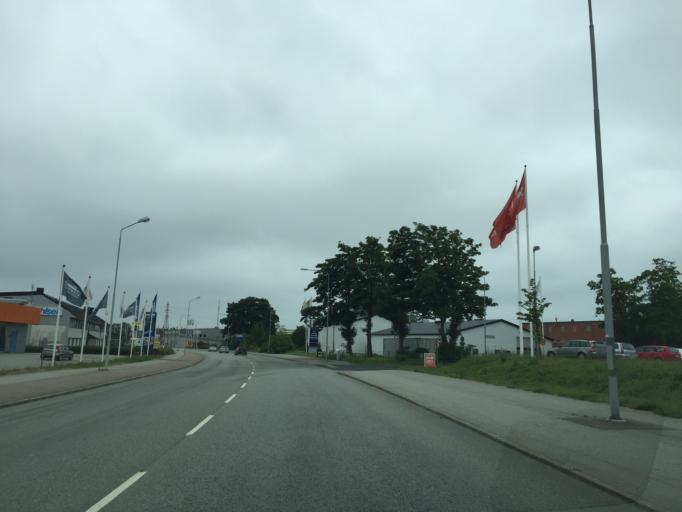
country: SE
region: Skane
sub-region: Ystads Kommun
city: Ystad
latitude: 55.4387
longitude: 13.8353
